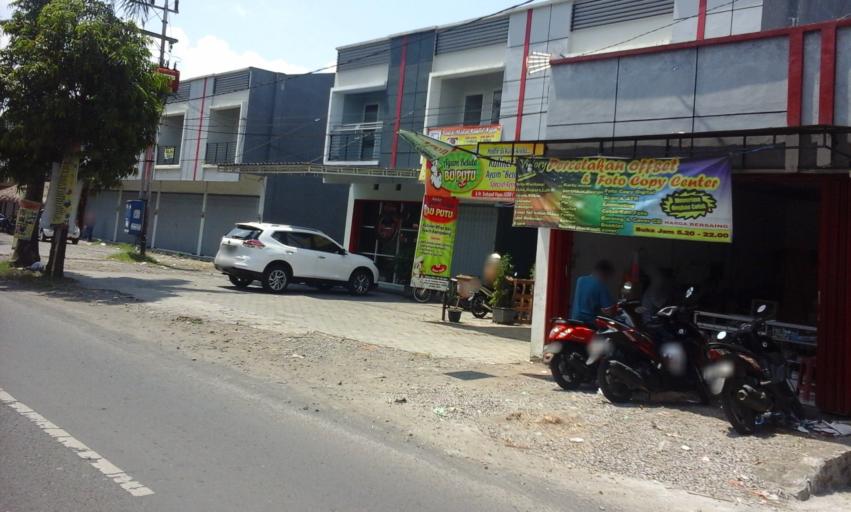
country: ID
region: East Java
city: Patrang
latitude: -8.1501
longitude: 113.7121
